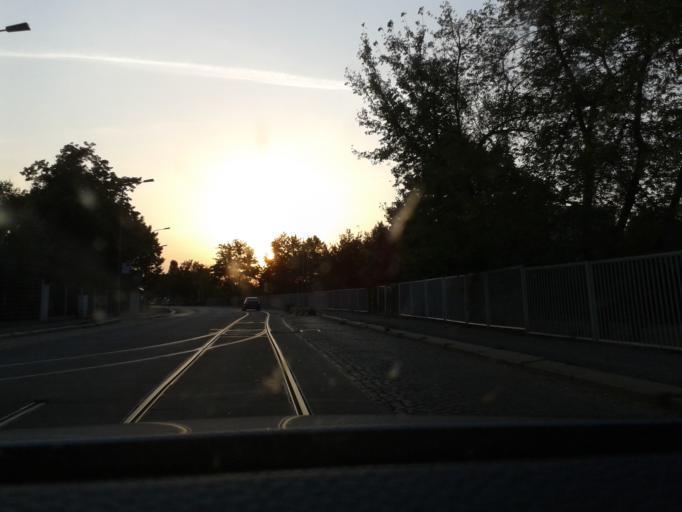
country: DE
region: Saxony
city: Heidenau
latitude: 51.0119
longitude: 13.8040
